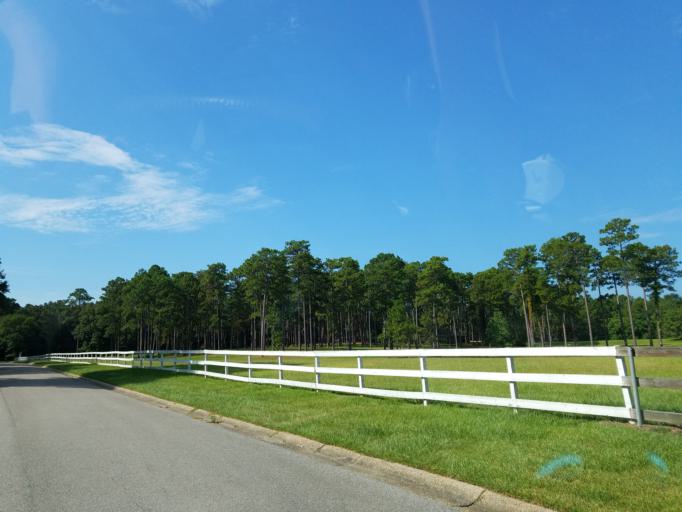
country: US
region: Mississippi
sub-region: Lamar County
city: West Hattiesburg
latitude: 31.3166
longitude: -89.3453
